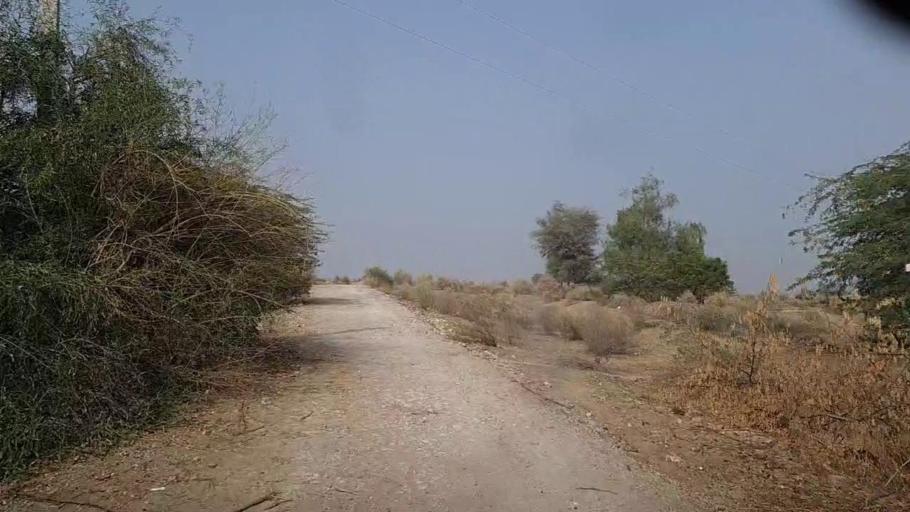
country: PK
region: Sindh
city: Bozdar
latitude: 27.0593
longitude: 68.6618
